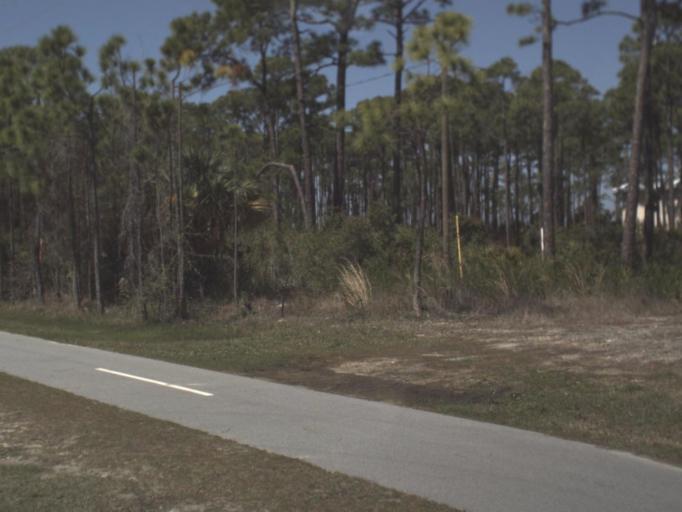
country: US
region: Florida
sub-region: Gulf County
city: Port Saint Joe
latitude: 29.6828
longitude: -85.3306
